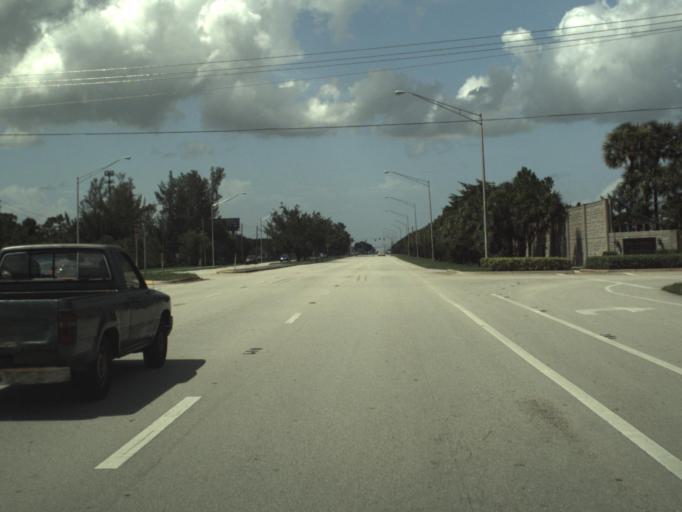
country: US
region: Florida
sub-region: Palm Beach County
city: Boca Del Mar
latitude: 26.3972
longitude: -80.2036
